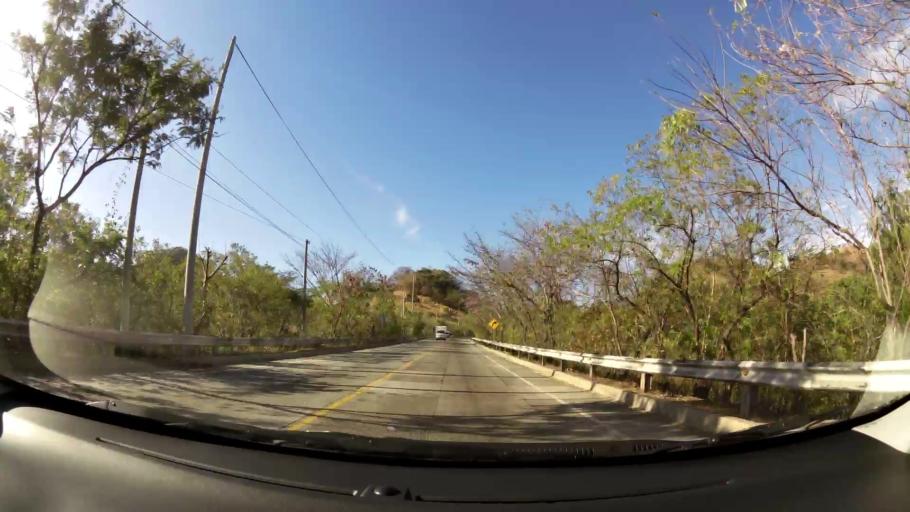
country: SV
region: Santa Ana
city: Texistepeque
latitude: 14.1429
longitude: -89.5136
